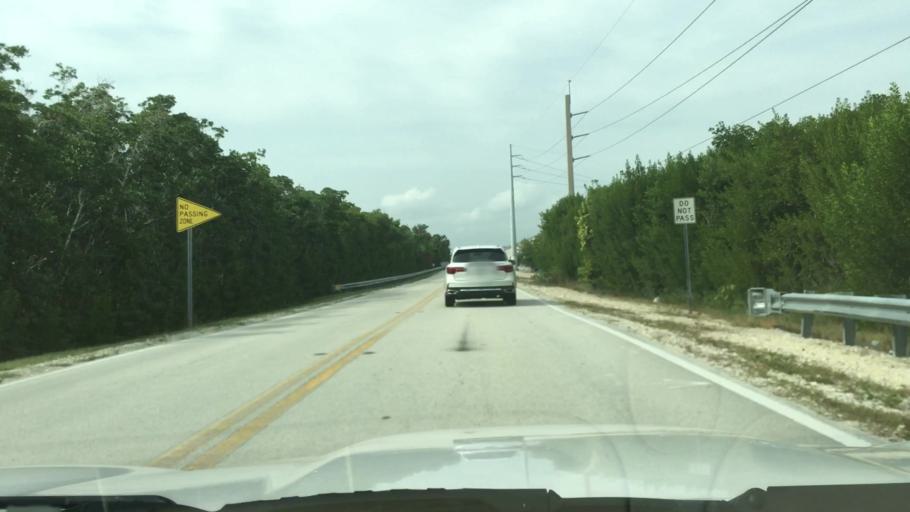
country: US
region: Florida
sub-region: Monroe County
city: North Key Largo
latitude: 25.2850
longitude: -80.3624
